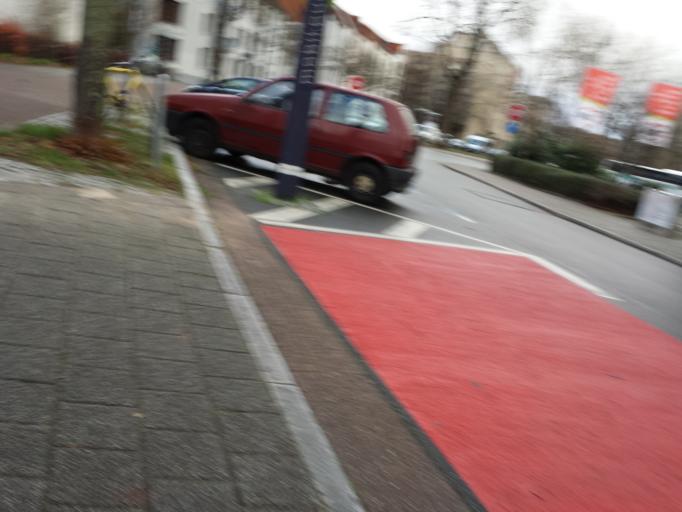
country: DE
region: Bremen
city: Bremen
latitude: 53.0759
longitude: 8.8194
